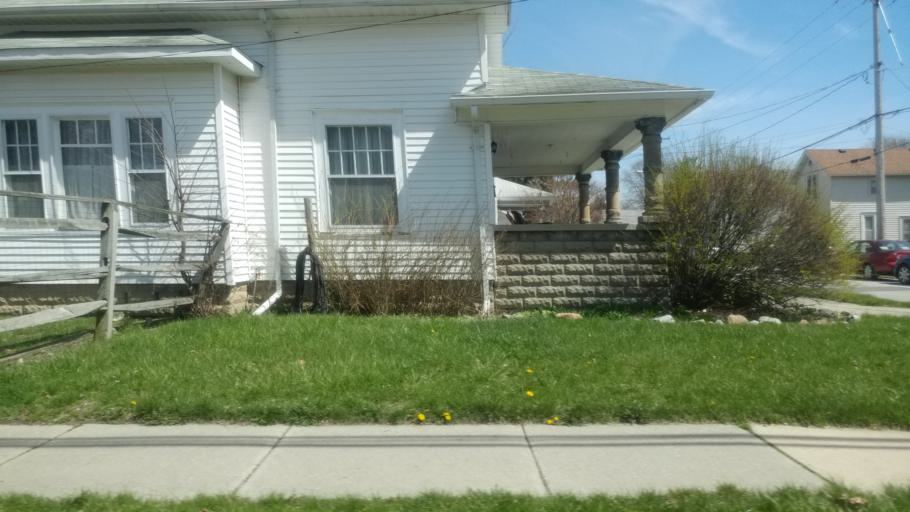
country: US
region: Ohio
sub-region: Wood County
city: Bowling Green
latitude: 41.3799
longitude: -83.6534
